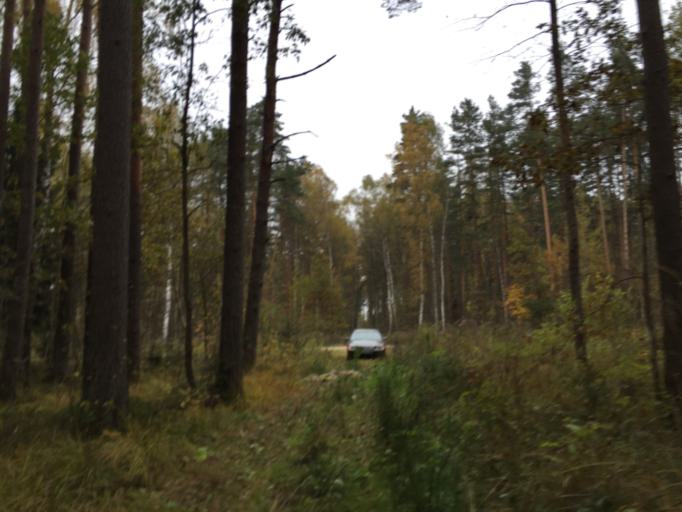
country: LV
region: Jelgava
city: Jelgava
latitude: 56.6372
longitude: 23.6406
